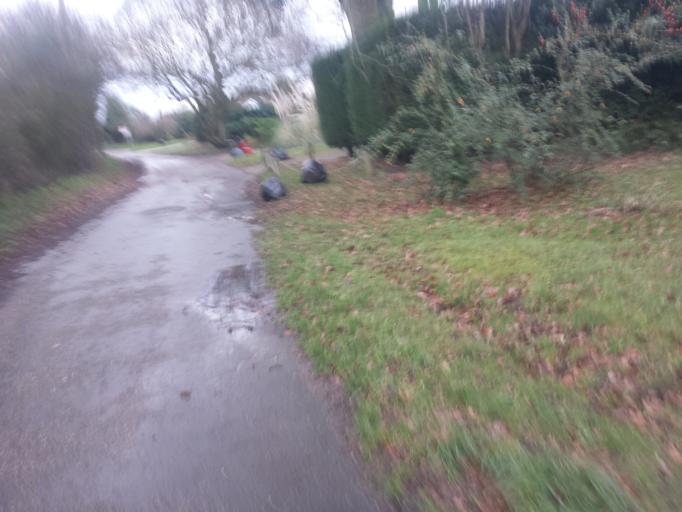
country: GB
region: England
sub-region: Essex
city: Great Bentley
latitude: 51.8839
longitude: 1.0370
